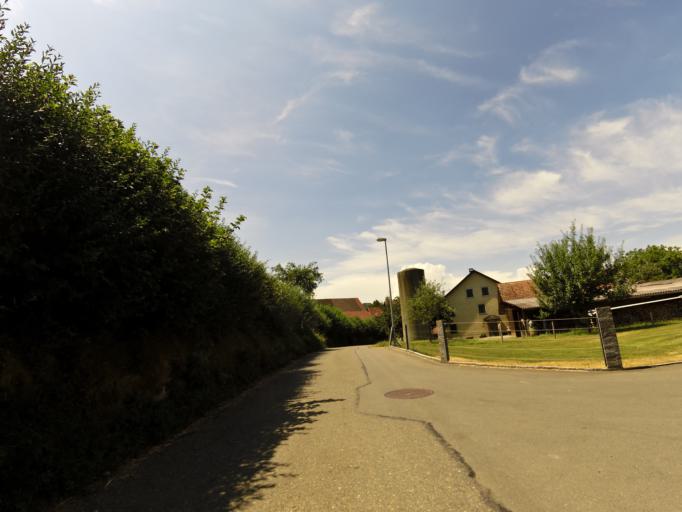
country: CH
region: Aargau
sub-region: Bezirk Bremgarten
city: Bremgarten
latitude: 47.3318
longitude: 8.3470
